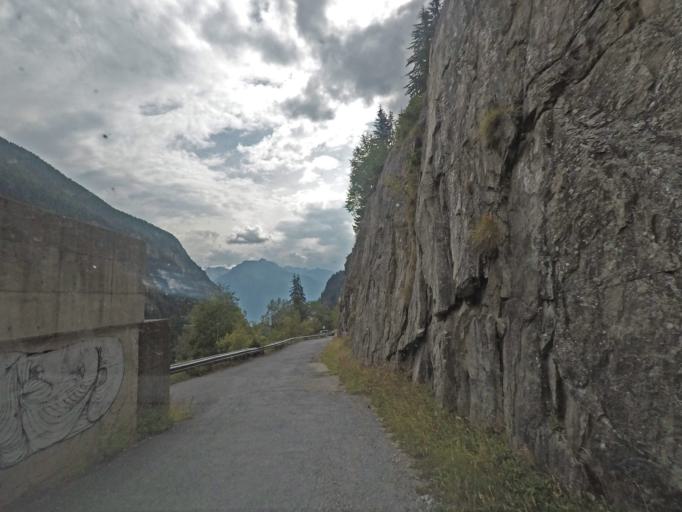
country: CH
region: Valais
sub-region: Brig District
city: Naters
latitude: 46.3693
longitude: 7.9999
